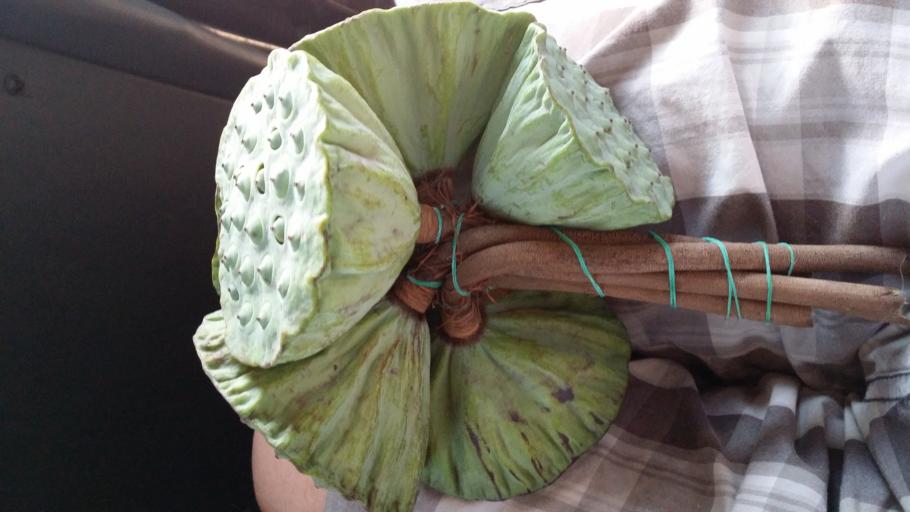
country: KH
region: Siem Reap
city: Siem Reap
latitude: 13.2990
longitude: 103.8400
